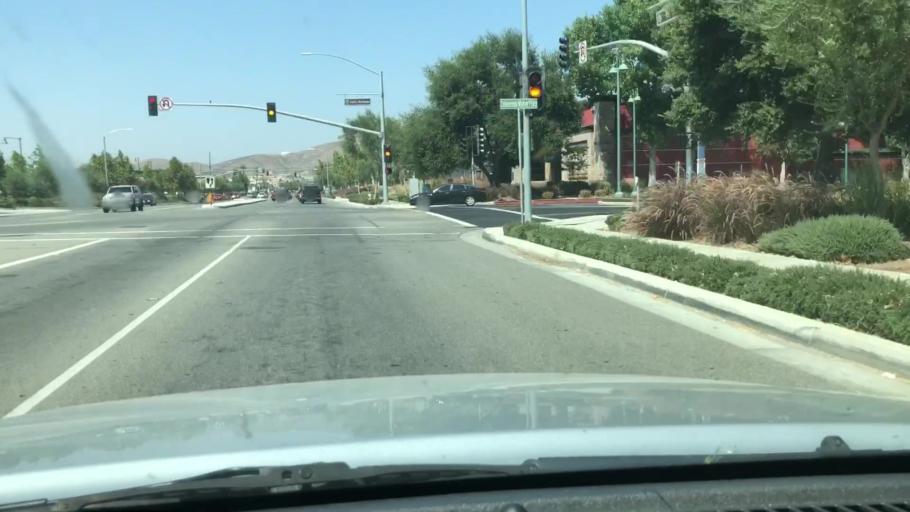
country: US
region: California
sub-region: Riverside County
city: Sun City
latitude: 33.6811
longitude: -117.1755
